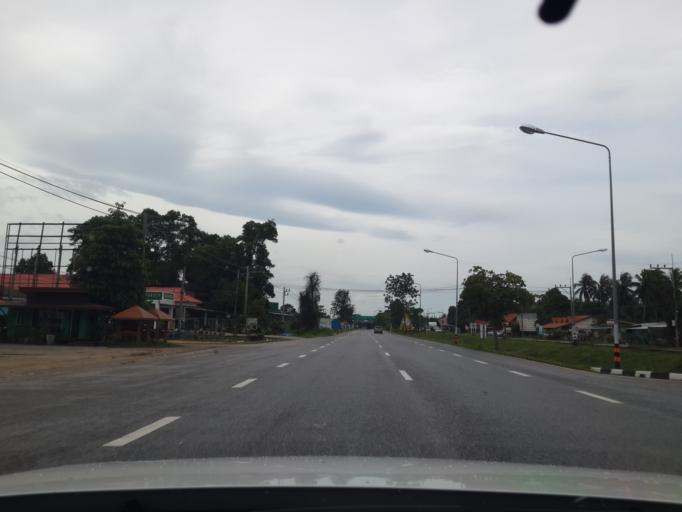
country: TH
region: Songkhla
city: Thepha
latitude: 6.8709
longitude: 100.9587
